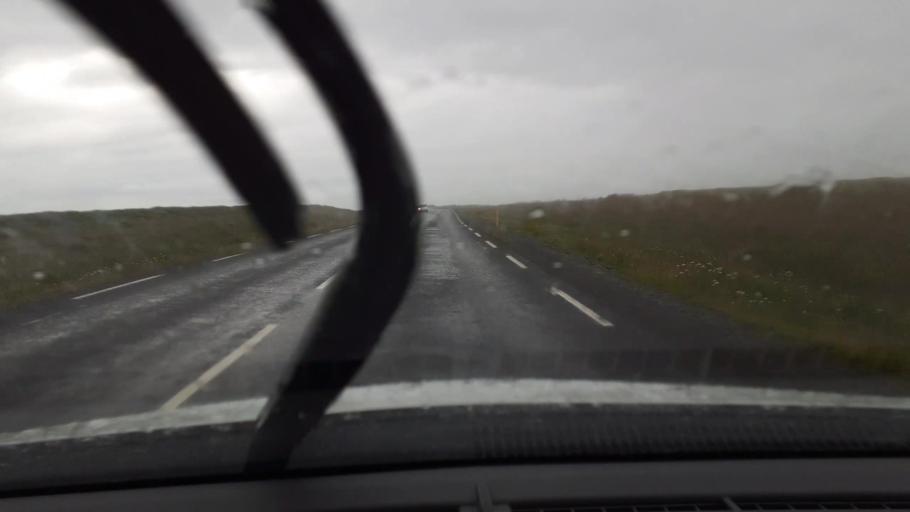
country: IS
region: West
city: Akranes
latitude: 64.3655
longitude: -21.9173
